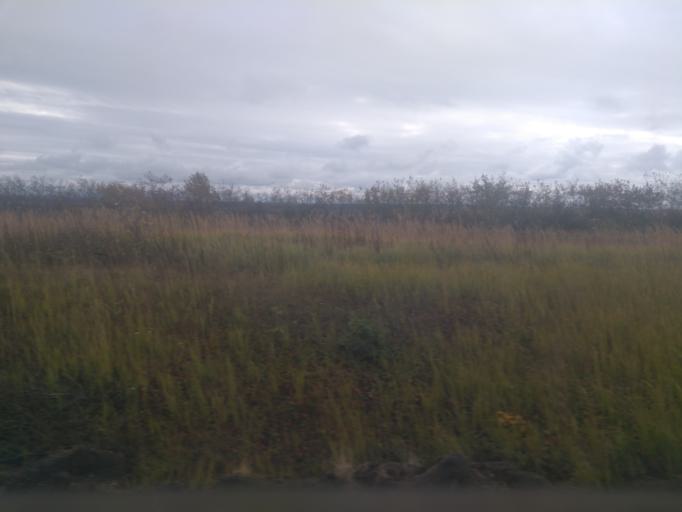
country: RU
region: Udmurtiya
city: Alnashi
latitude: 56.2185
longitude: 52.6455
